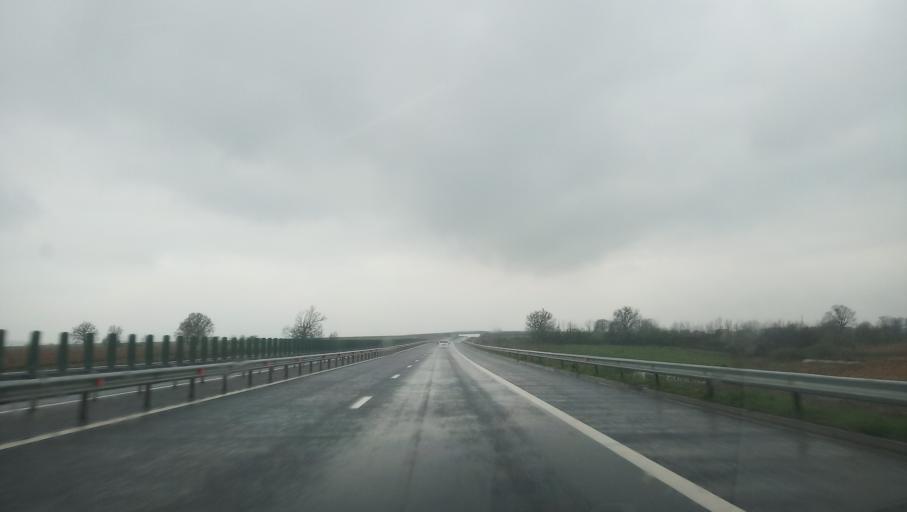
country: RO
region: Timis
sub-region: Comuna Faget
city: Faget
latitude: 45.8316
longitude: 22.2062
